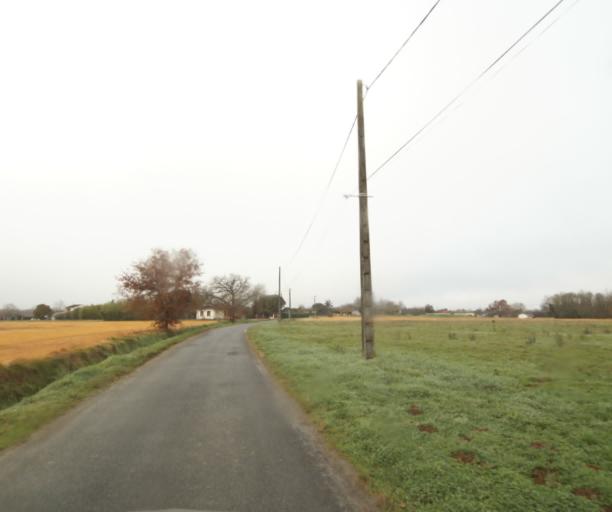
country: FR
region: Midi-Pyrenees
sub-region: Departement du Tarn-et-Garonne
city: Nohic
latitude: 43.8795
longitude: 1.4635
